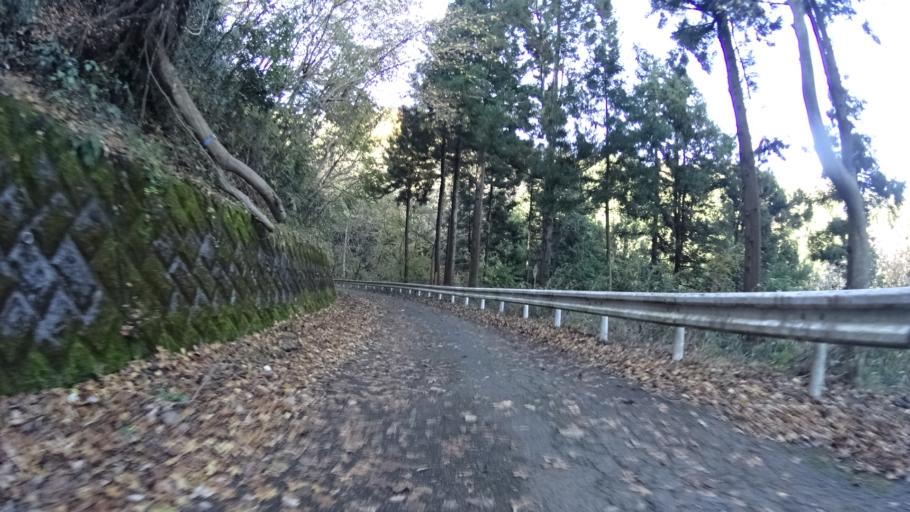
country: JP
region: Kanagawa
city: Zama
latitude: 35.5255
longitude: 139.2728
